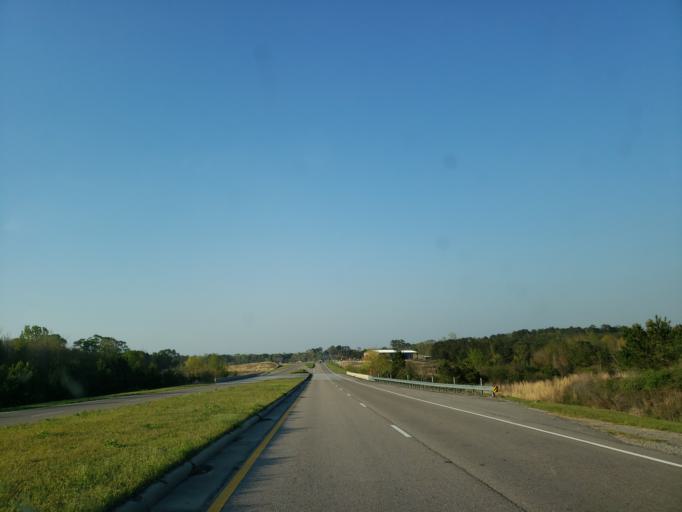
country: US
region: Mississippi
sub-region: Lauderdale County
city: Marion
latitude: 32.3848
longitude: -88.6542
